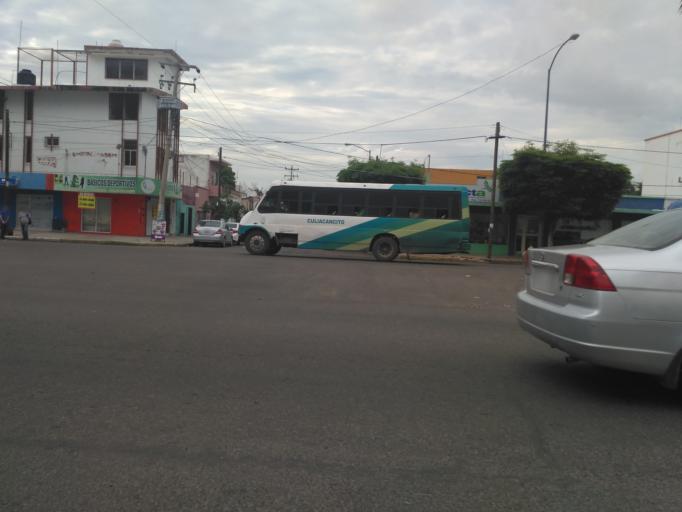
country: MX
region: Sinaloa
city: Culiacan
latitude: 24.8014
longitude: -107.3976
